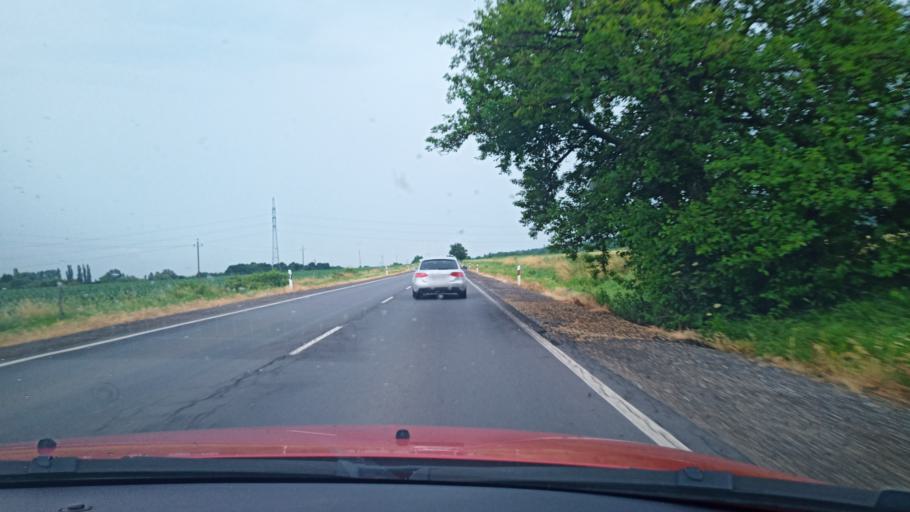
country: HU
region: Borsod-Abauj-Zemplen
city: Malyi
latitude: 48.0442
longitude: 20.8028
